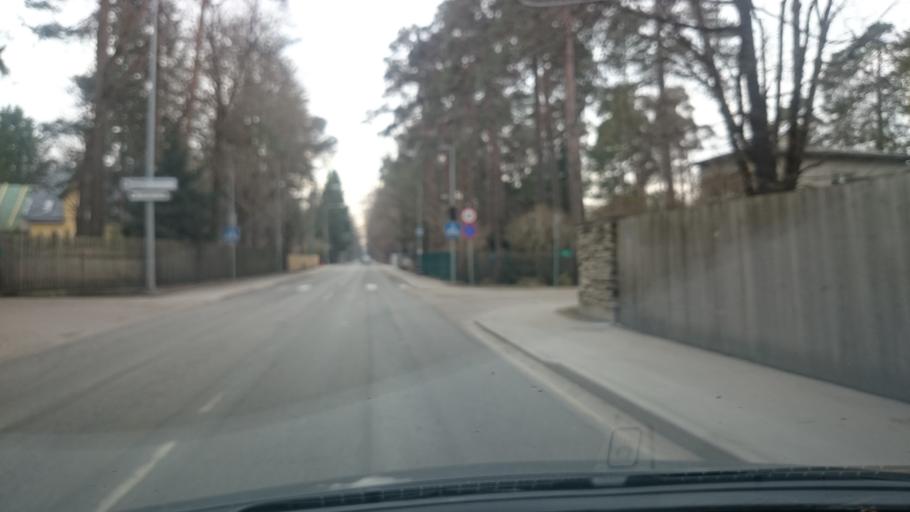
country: EE
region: Harju
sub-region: Saue vald
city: Laagri
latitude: 59.3757
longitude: 24.6347
